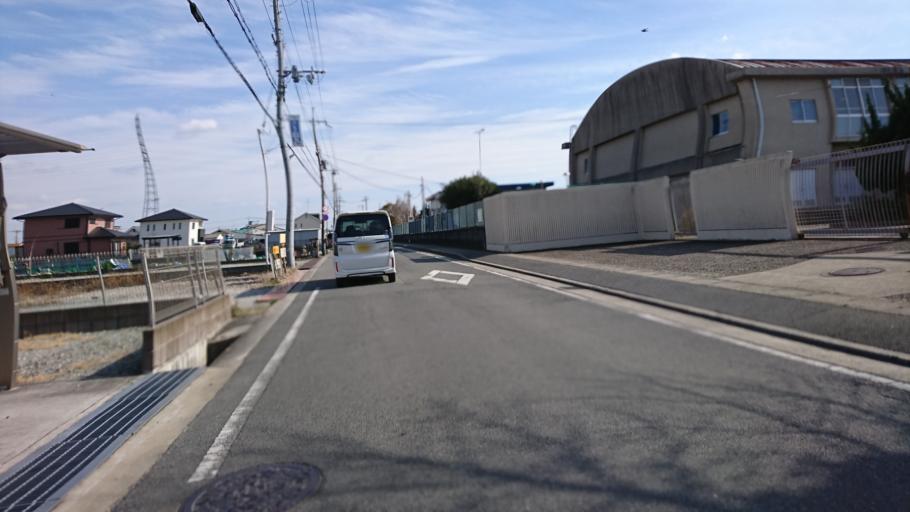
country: JP
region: Hyogo
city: Kakogawacho-honmachi
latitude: 34.7882
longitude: 134.8275
